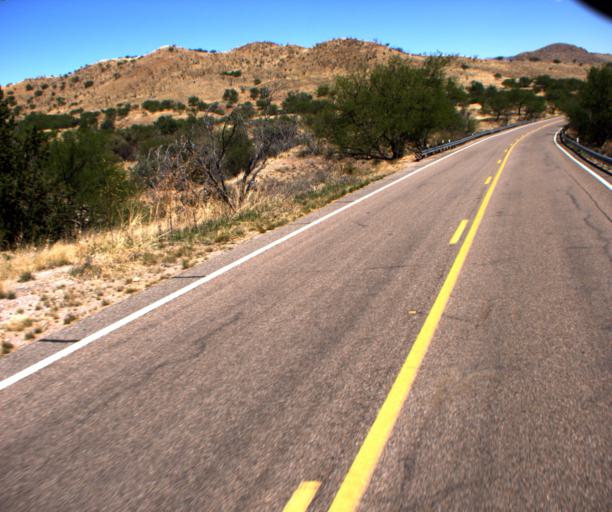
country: US
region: Arizona
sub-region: Santa Cruz County
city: Rio Rico
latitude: 31.4742
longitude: -110.8203
